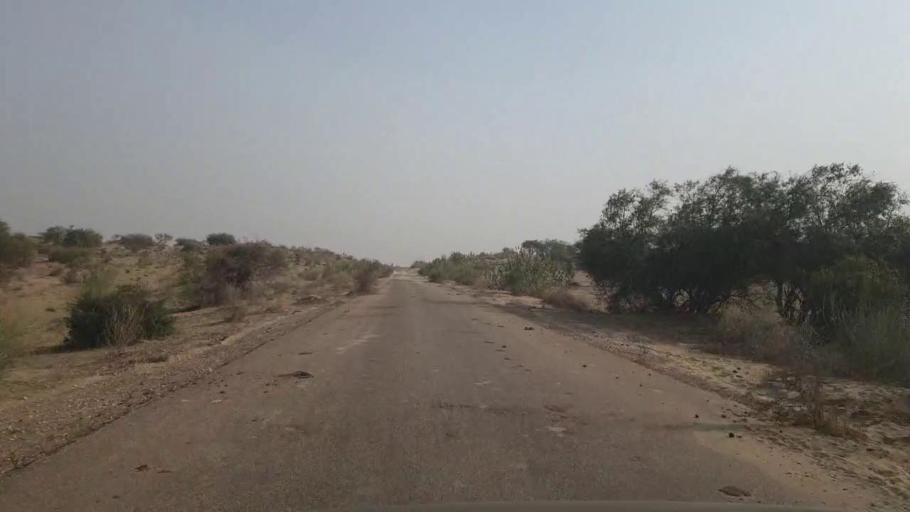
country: PK
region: Sindh
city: Chor
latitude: 25.5109
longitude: 69.9672
